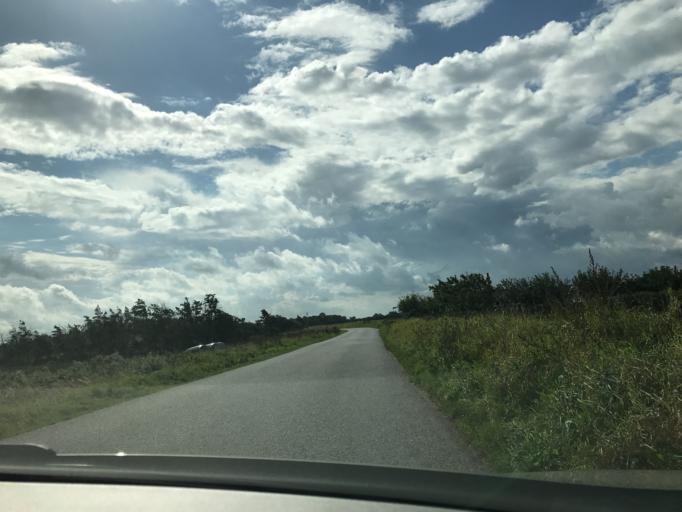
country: DK
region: South Denmark
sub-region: Middelfart Kommune
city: Norre Aby
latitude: 55.4240
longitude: 9.8294
